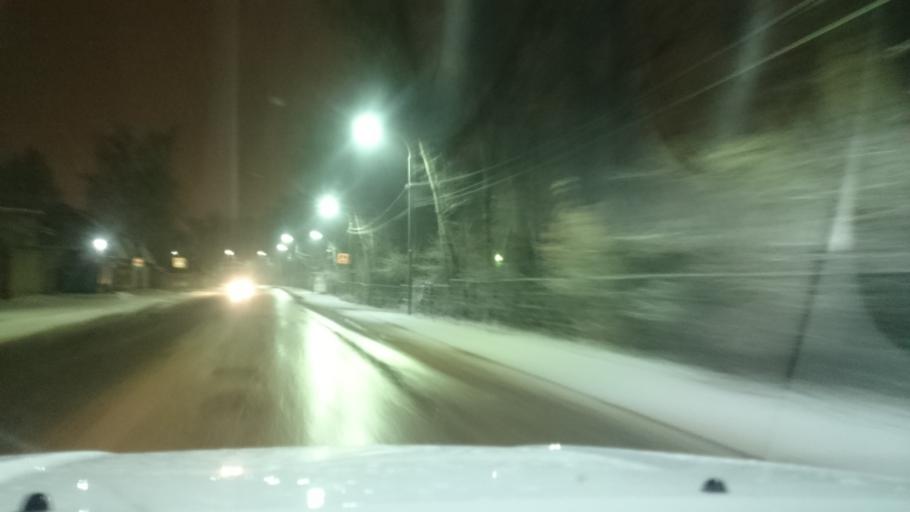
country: RU
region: Tula
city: Gorelki
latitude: 54.2240
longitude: 37.5831
